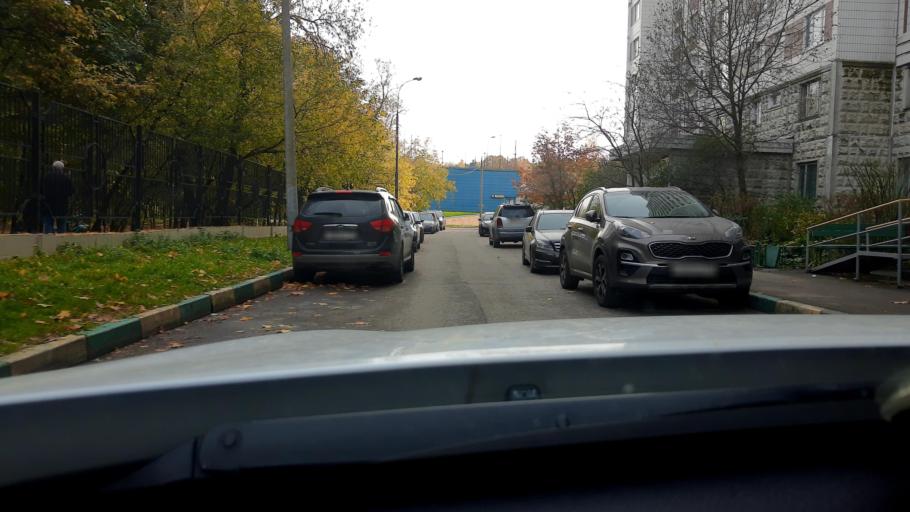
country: RU
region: Moskovskaya
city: Bol'shaya Setun'
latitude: 55.7401
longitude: 37.4384
